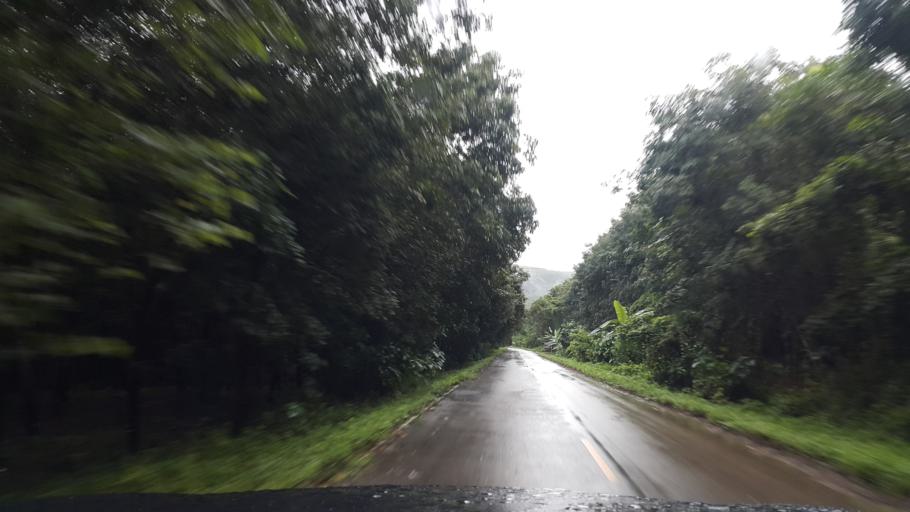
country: TH
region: Phayao
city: Phu Sang
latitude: 19.6157
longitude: 100.4065
